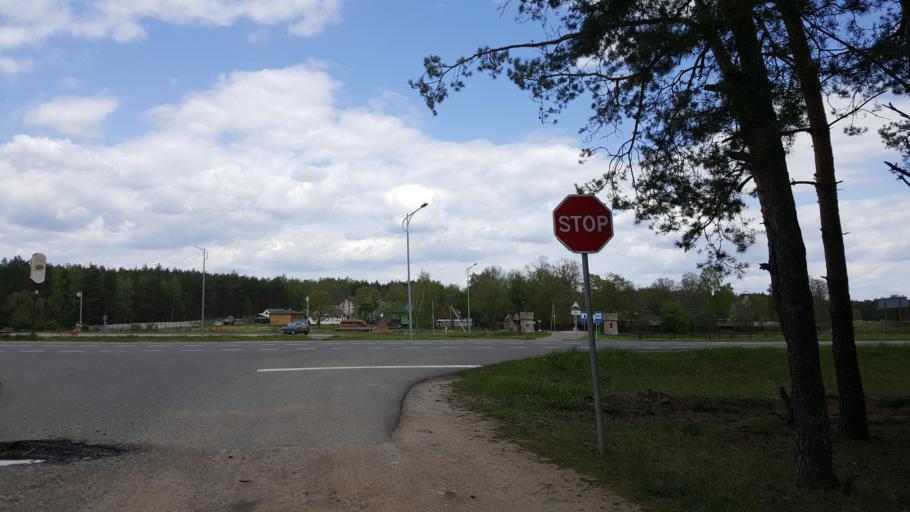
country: BY
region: Brest
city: Zhabinka
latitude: 52.4024
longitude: 24.0887
